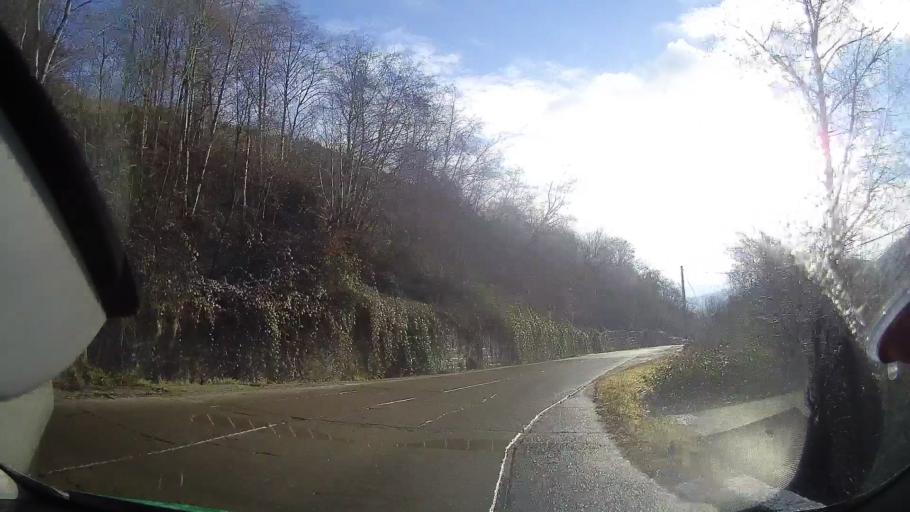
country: RO
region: Alba
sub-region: Comuna Sohodol
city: Sohodol
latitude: 46.3798
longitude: 23.0131
